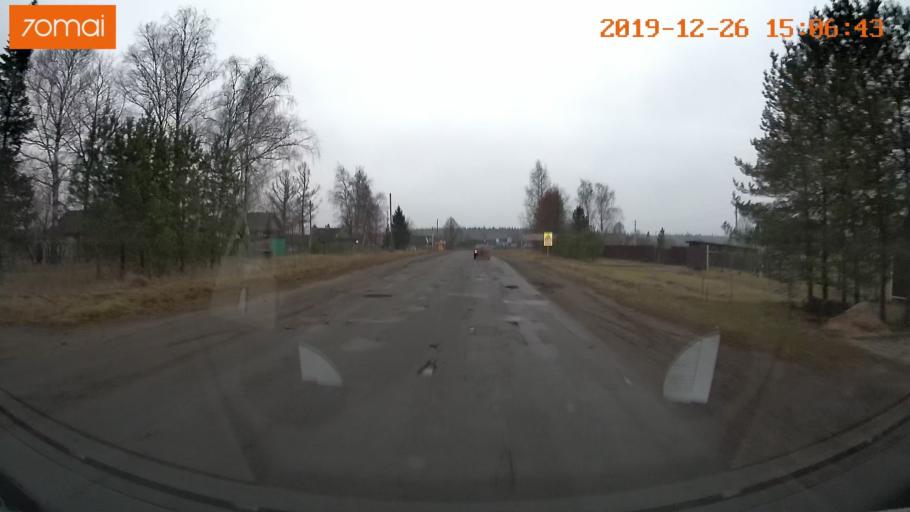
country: RU
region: Jaroslavl
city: Rybinsk
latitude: 58.1760
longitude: 38.8440
